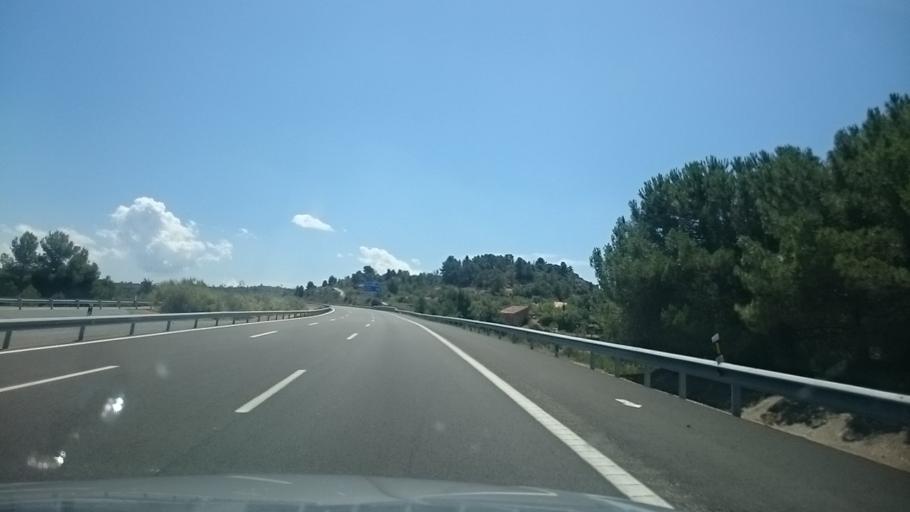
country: ES
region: Catalonia
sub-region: Provincia de Lleida
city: Vinaixa
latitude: 41.4349
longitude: 0.9249
